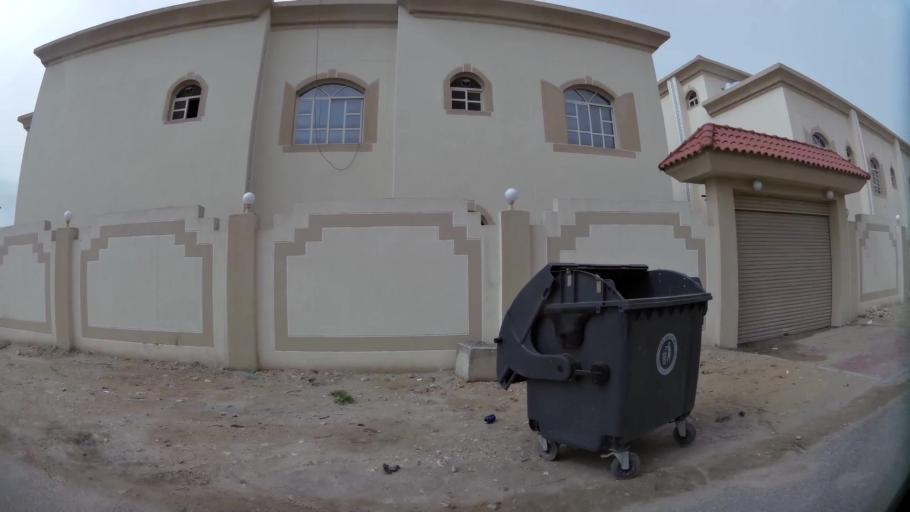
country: QA
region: Baladiyat ad Dawhah
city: Doha
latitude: 25.2421
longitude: 51.5387
